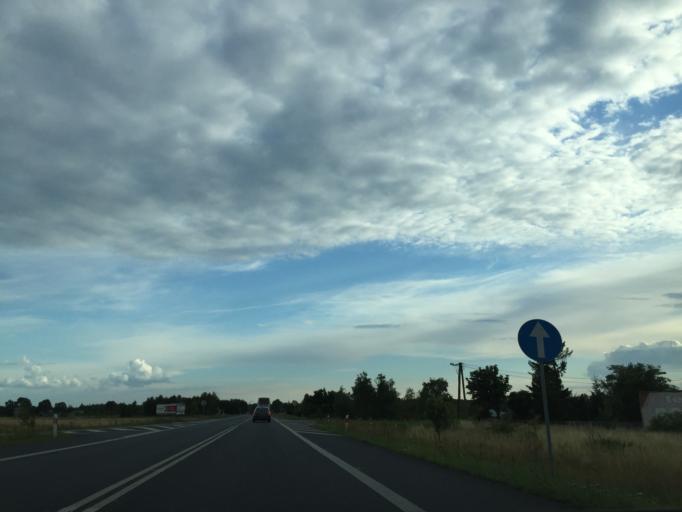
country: PL
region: Lublin Voivodeship
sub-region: Powiat lubartowski
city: Lubartow
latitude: 51.4693
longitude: 22.5817
